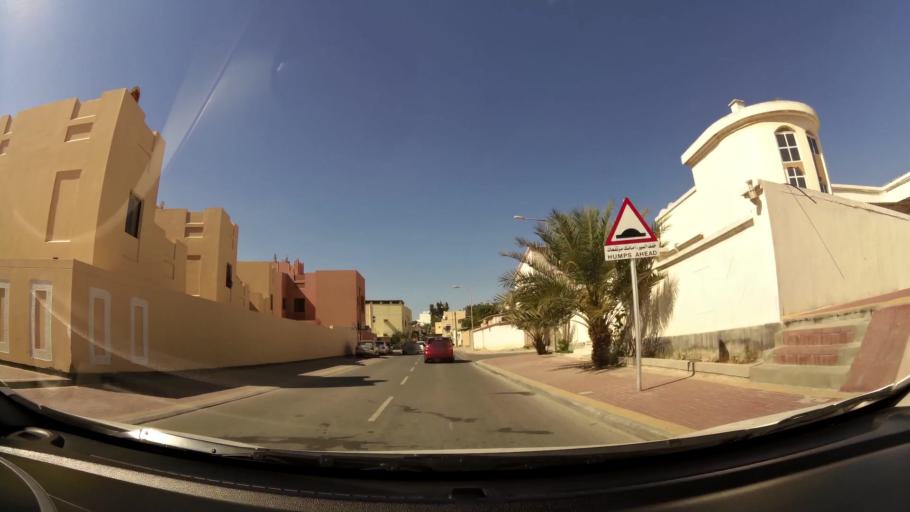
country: BH
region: Muharraq
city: Al Muharraq
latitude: 26.2502
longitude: 50.6320
